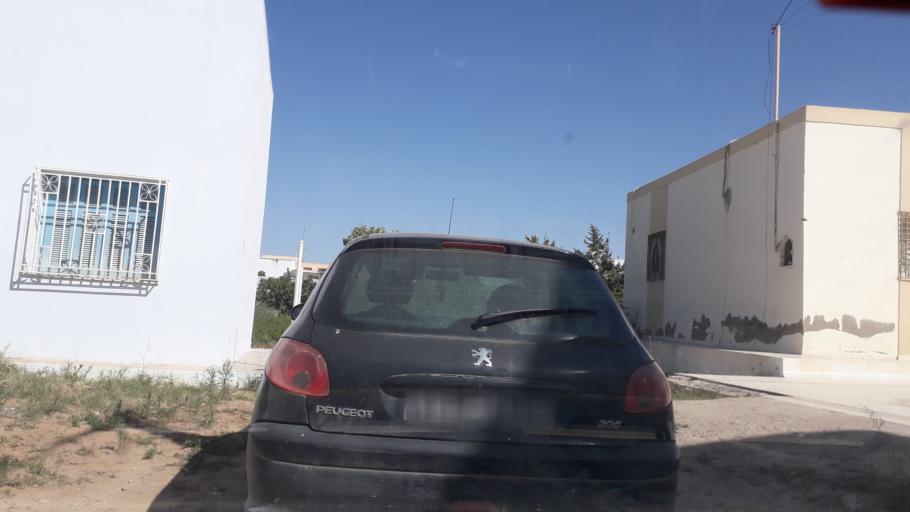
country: TN
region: Safaqis
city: Al Qarmadah
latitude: 34.8080
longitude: 10.7659
